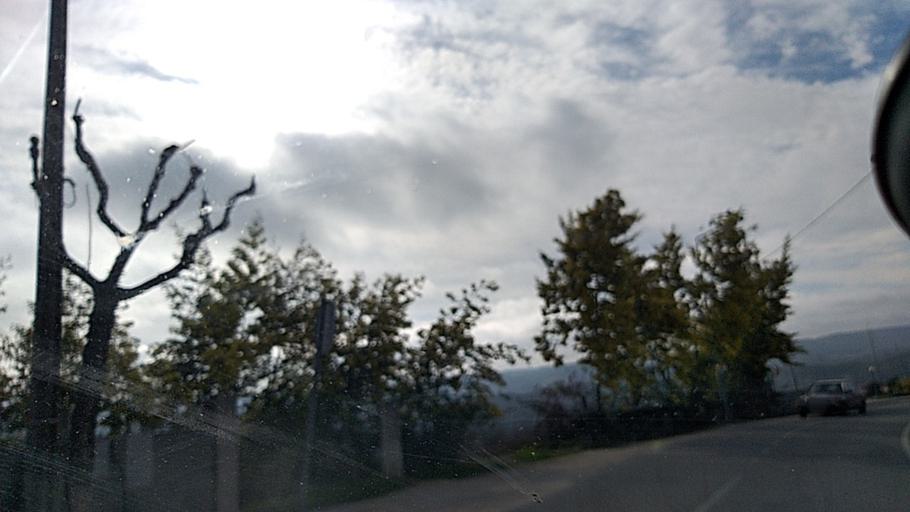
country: PT
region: Guarda
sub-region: Aguiar da Beira
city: Aguiar da Beira
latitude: 40.7397
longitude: -7.5548
